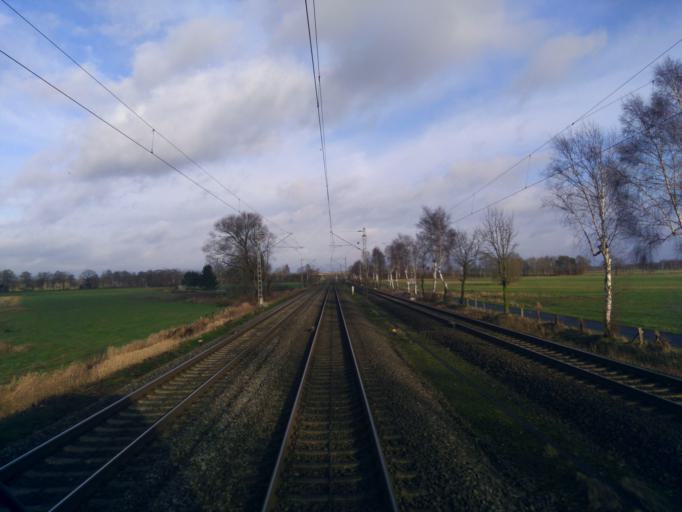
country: DE
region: Lower Saxony
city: Scheessel
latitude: 53.1775
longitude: 9.5127
